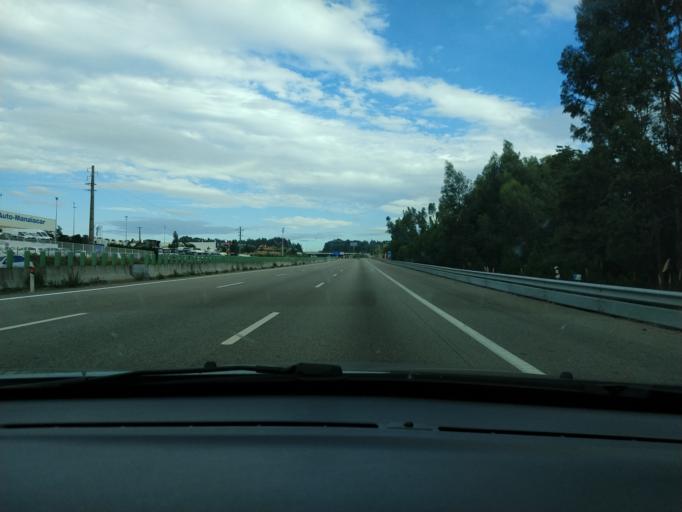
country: PT
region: Aveiro
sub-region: Santa Maria da Feira
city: Feira
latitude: 40.9177
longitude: -8.5676
